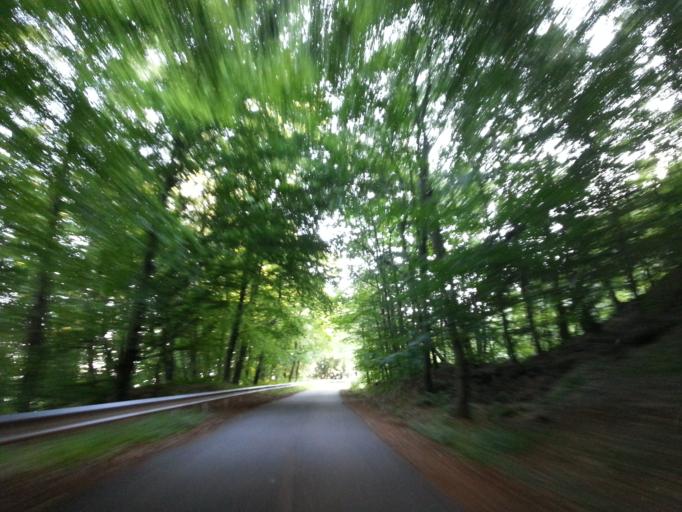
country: FR
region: Alsace
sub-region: Departement du Bas-Rhin
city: Lembach
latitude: 48.9782
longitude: 7.8287
